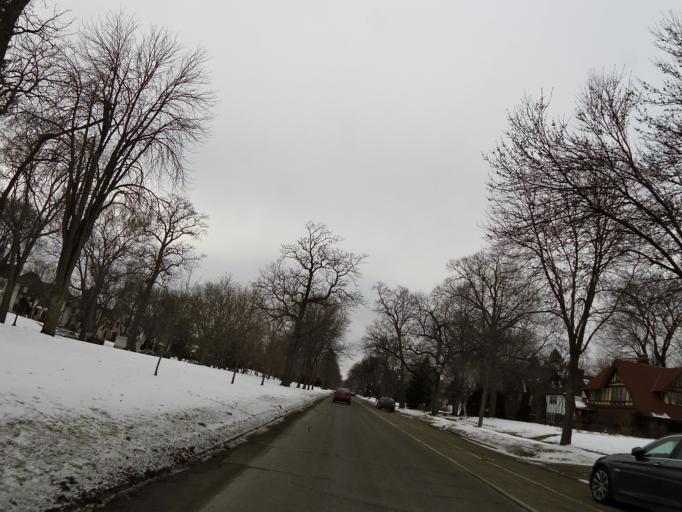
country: US
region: Minnesota
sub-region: Ramsey County
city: Falcon Heights
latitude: 44.9417
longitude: -93.1791
